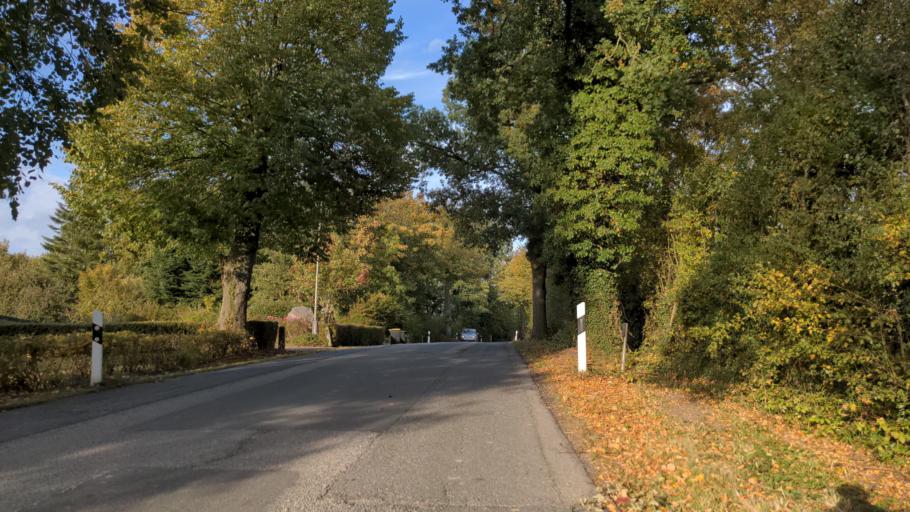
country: DE
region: Schleswig-Holstein
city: Ahrensbok
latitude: 53.9901
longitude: 10.5733
